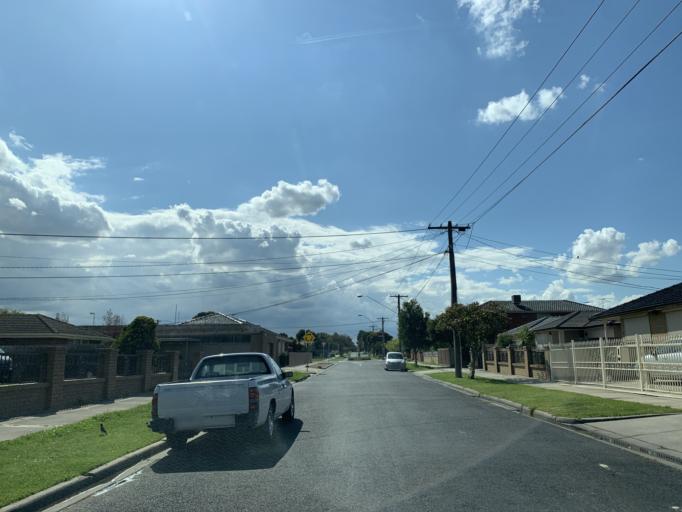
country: AU
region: Victoria
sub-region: Brimbank
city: Kealba
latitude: -37.7455
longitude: 144.8255
